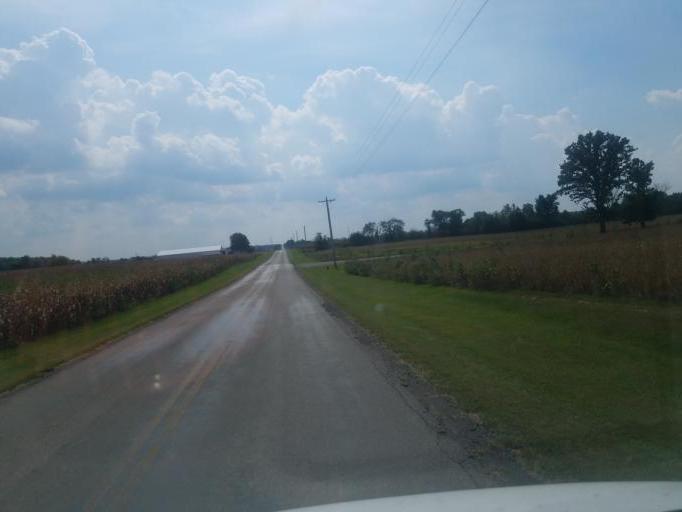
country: US
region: Ohio
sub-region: Logan County
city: Northwood
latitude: 40.6230
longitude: -83.7629
